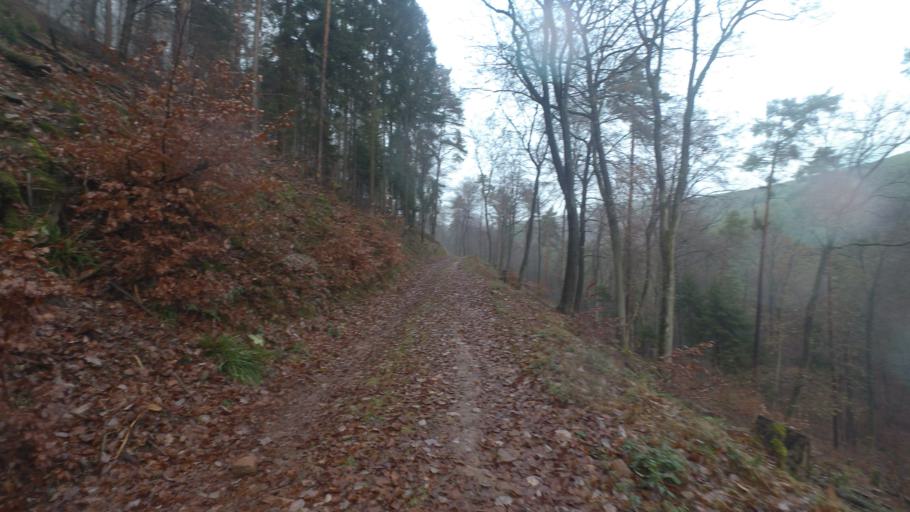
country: DE
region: Rheinland-Pfalz
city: Deidesheim
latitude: 49.4067
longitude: 8.1477
